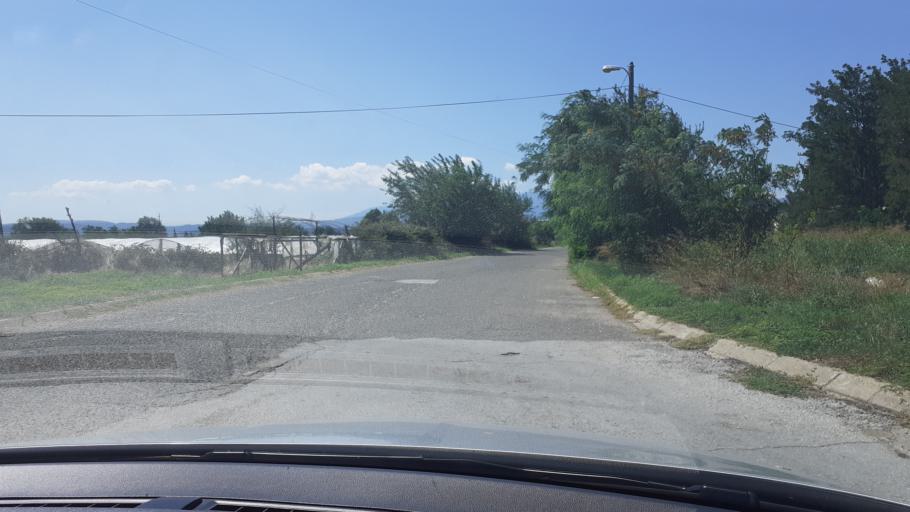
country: MK
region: Bogdanci
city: Bogdanci
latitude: 41.2022
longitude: 22.5864
